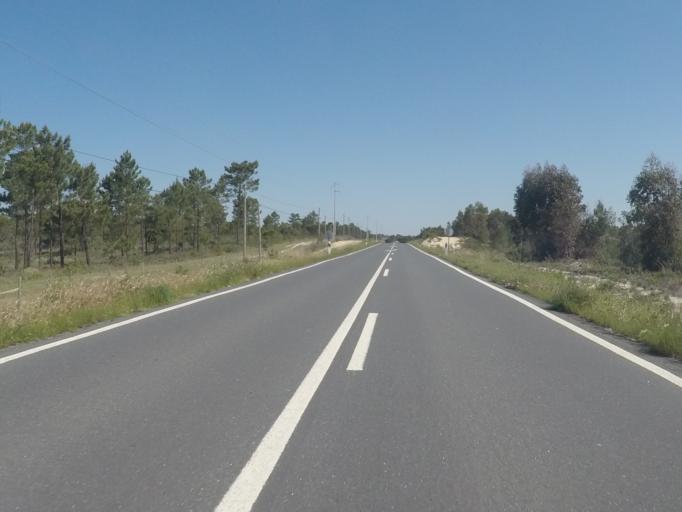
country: PT
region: Setubal
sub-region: Grandola
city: Grandola
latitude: 38.2432
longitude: -8.7374
